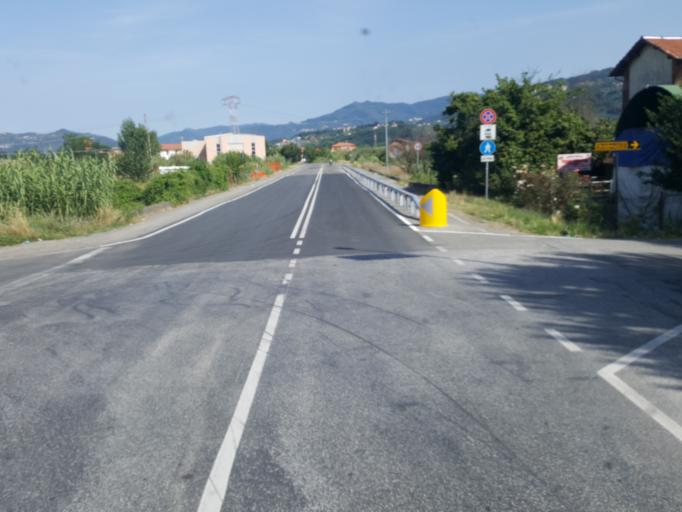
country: IT
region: Liguria
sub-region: Provincia di La Spezia
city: Santo Stefano di Magra
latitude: 44.1545
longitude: 9.9125
